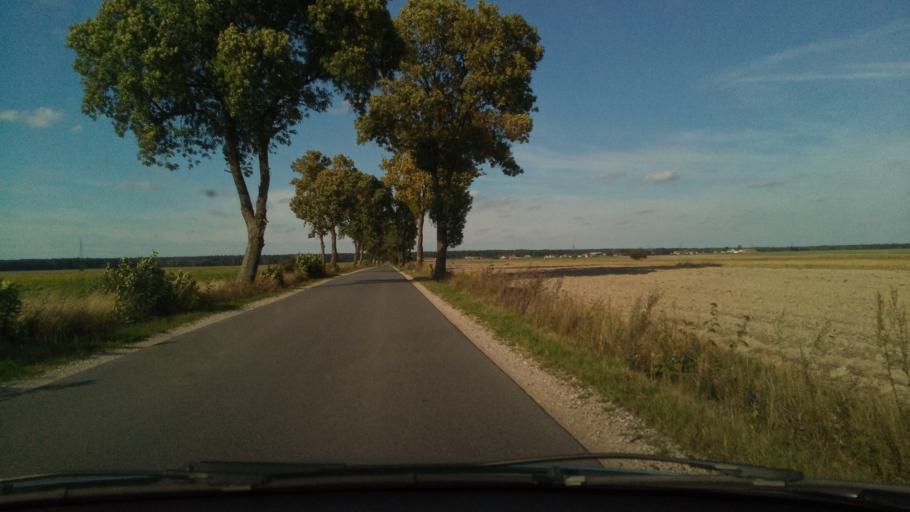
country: PL
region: Lodz Voivodeship
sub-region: Powiat piotrkowski
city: Sulejow
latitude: 51.3894
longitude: 19.8203
